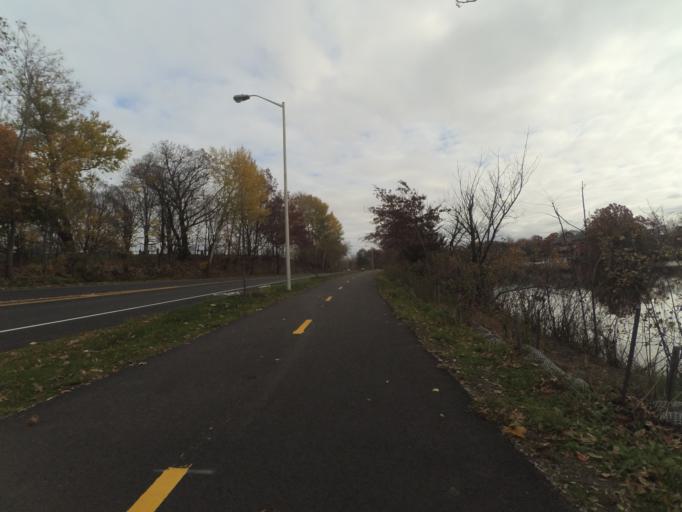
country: US
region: Massachusetts
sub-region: Middlesex County
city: Cambridge
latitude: 42.3655
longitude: -71.1429
